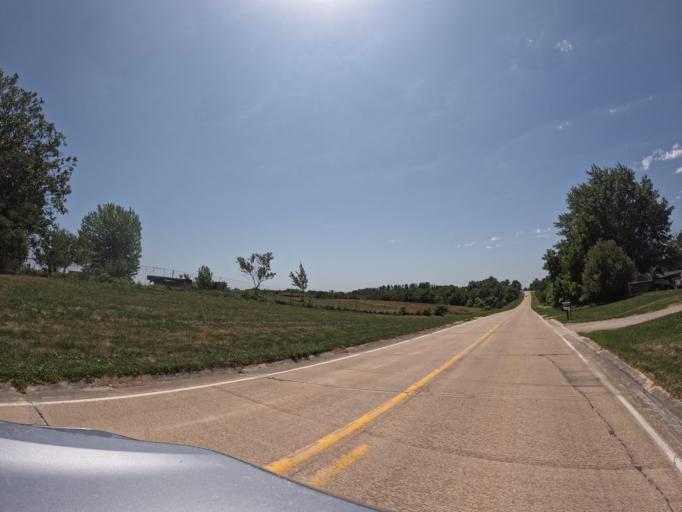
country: US
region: Iowa
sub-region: Henry County
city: Mount Pleasant
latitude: 40.9513
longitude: -91.5545
